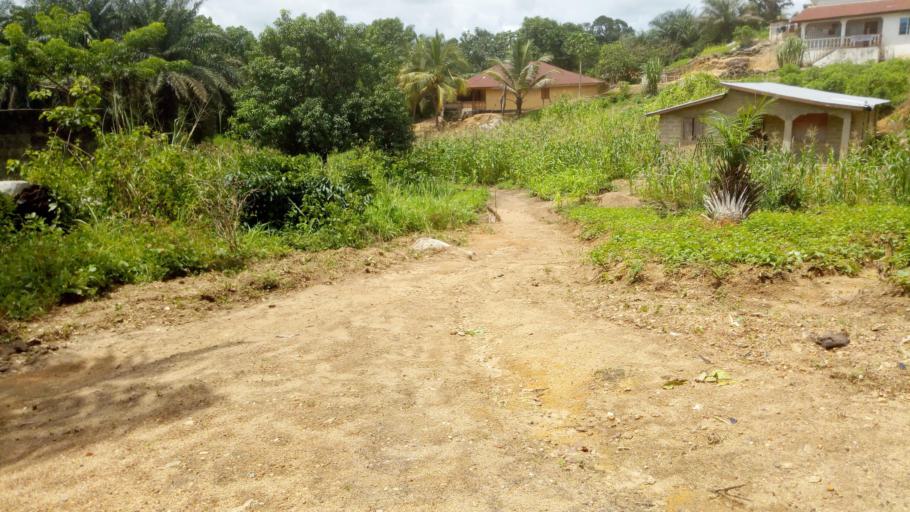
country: SL
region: Northern Province
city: Magburaka
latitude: 8.7236
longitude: -11.9546
